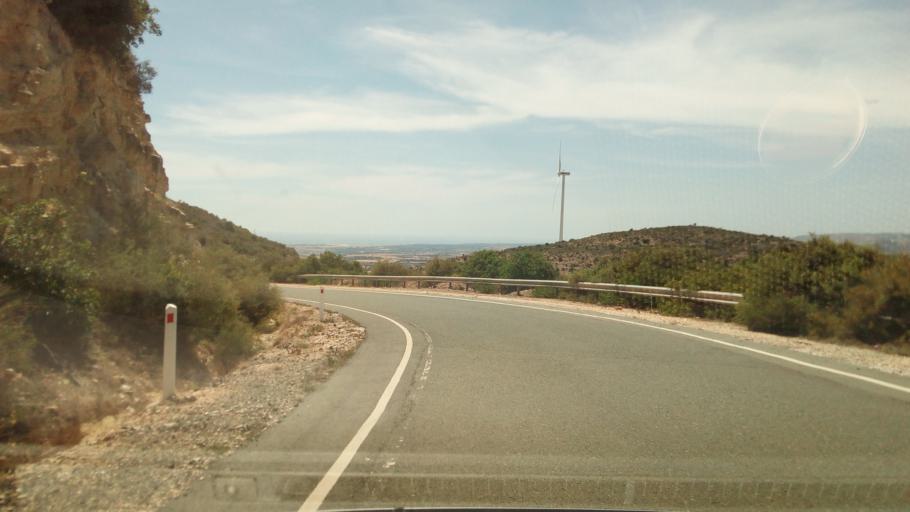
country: CY
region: Limassol
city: Pissouri
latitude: 34.7266
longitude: 32.6180
